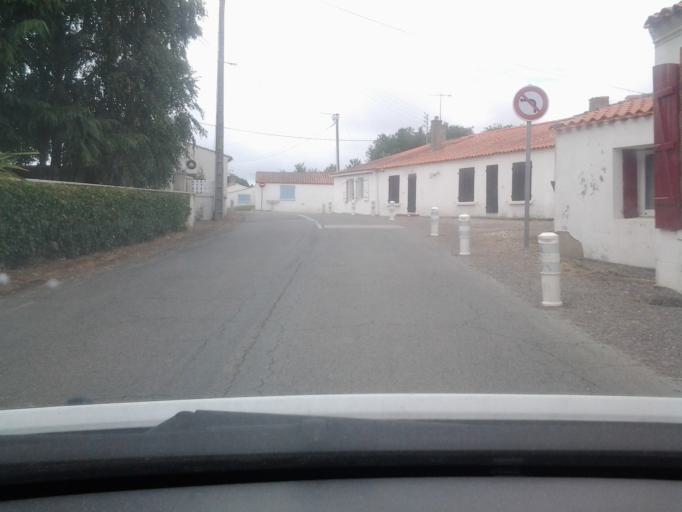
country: FR
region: Pays de la Loire
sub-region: Departement de la Vendee
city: Angles
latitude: 46.3940
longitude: -1.4068
